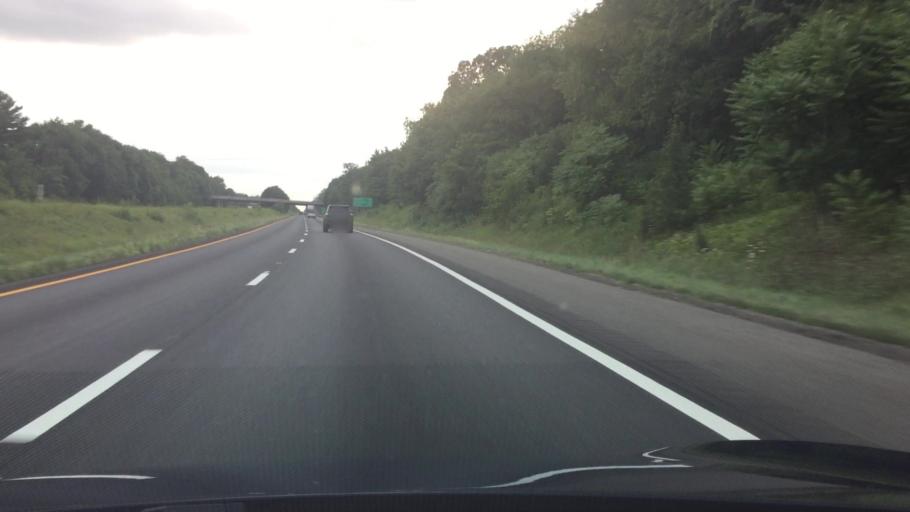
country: US
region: Virginia
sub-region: Montgomery County
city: Christiansburg
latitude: 37.1241
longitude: -80.3953
